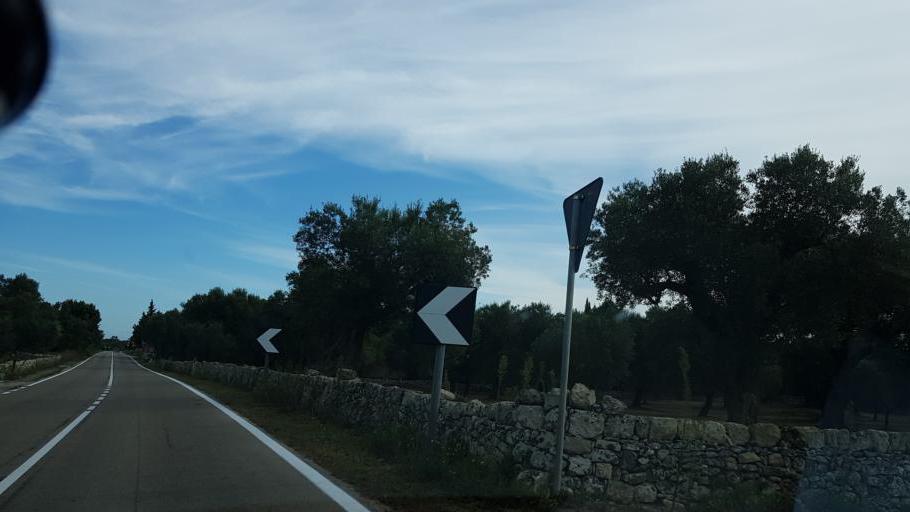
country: IT
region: Apulia
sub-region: Provincia di Lecce
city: Melendugno
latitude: 40.3315
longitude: 18.3445
